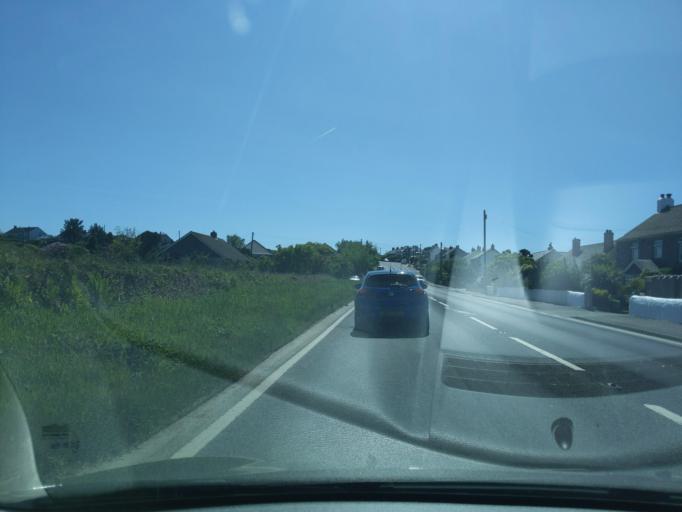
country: GB
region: England
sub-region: Cornwall
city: Perranarworthal
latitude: 50.1637
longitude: -5.1796
